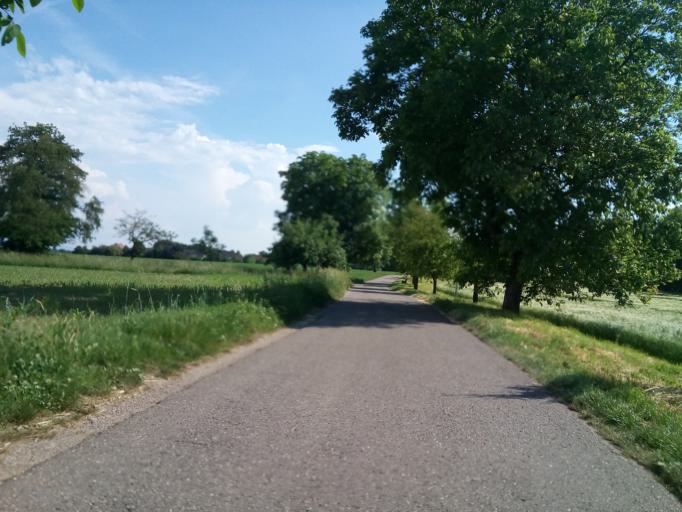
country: DE
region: Baden-Wuerttemberg
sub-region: Karlsruhe Region
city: Lichtenau
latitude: 48.7176
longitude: 8.0021
